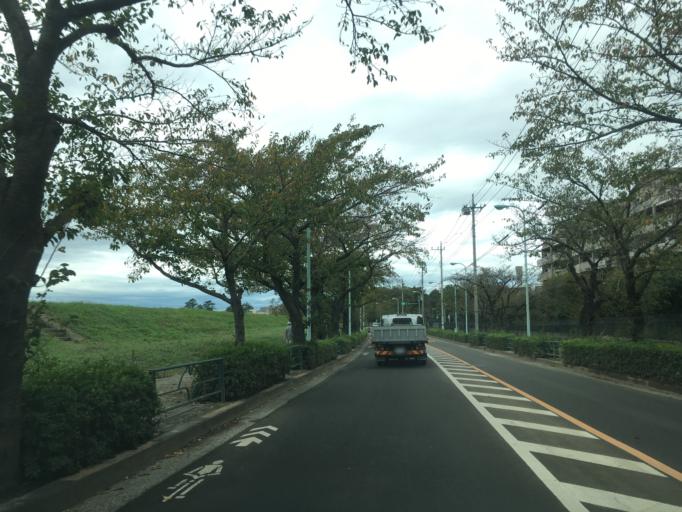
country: JP
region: Tokyo
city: Chofugaoka
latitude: 35.6343
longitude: 139.5646
